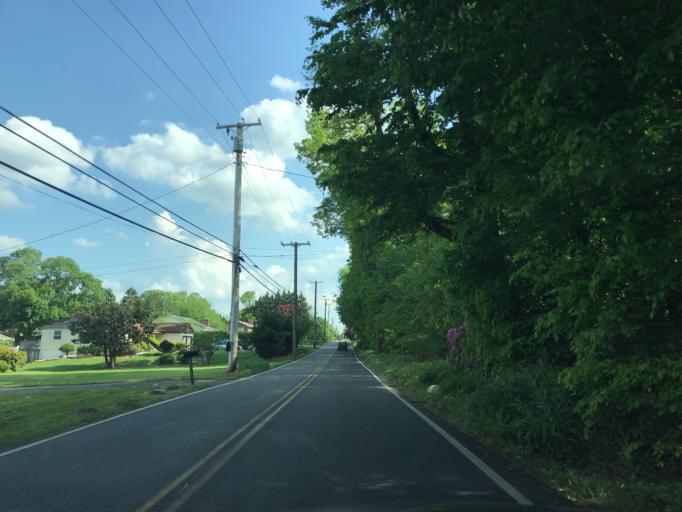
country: US
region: Maryland
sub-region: Harford County
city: Bel Air North
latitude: 39.5592
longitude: -76.3984
